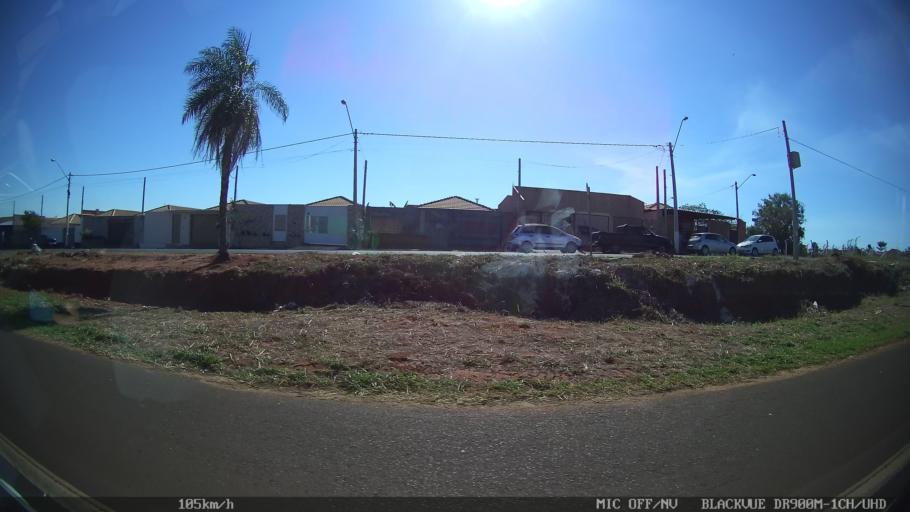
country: BR
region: Sao Paulo
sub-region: Olimpia
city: Olimpia
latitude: -20.7334
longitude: -48.8732
